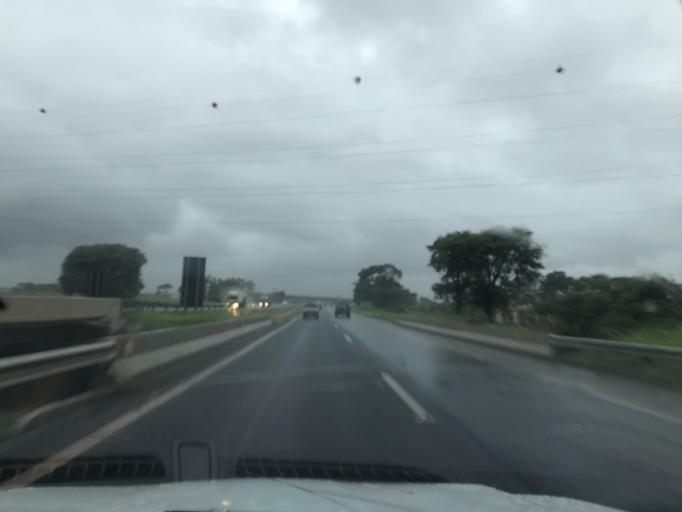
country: BR
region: Sao Paulo
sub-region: Ribeirao Preto
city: Ribeirao Preto
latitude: -21.1079
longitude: -47.7838
